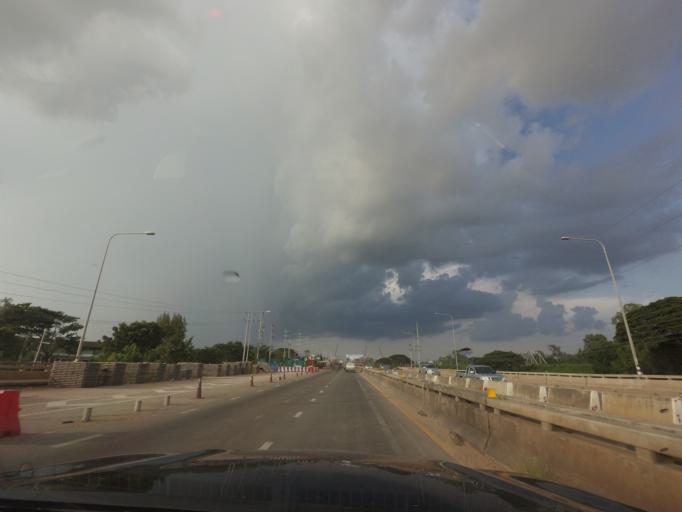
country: TH
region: Khon Kaen
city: Khon Kaen
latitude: 16.3701
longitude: 102.8083
